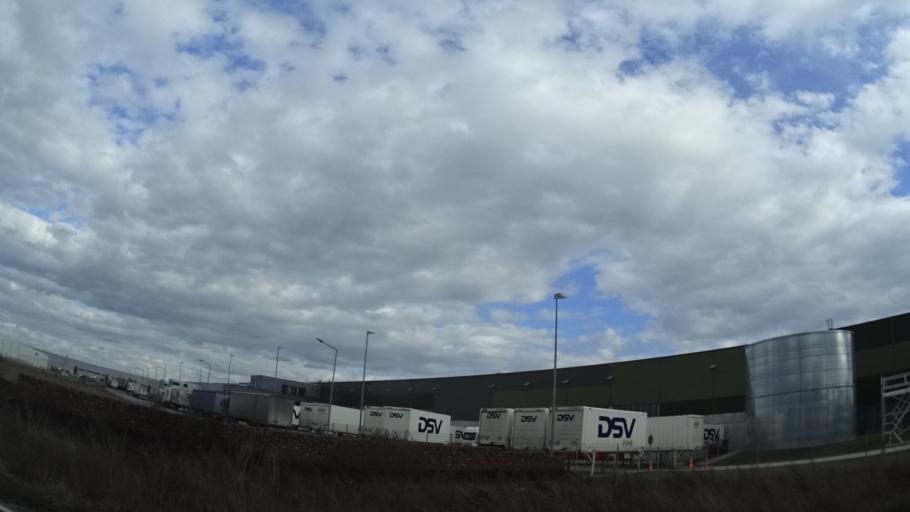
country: DE
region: Hesse
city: Gernsheim
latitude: 49.7658
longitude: 8.4945
